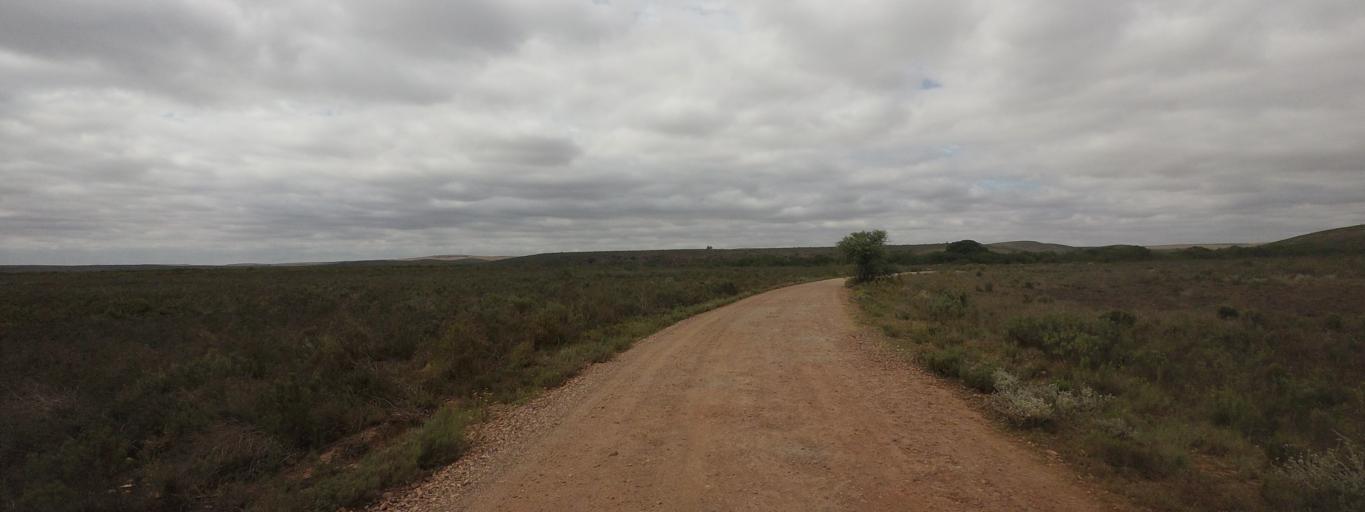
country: ZA
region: Western Cape
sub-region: Overberg District Municipality
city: Swellendam
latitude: -34.0639
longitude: 20.4389
